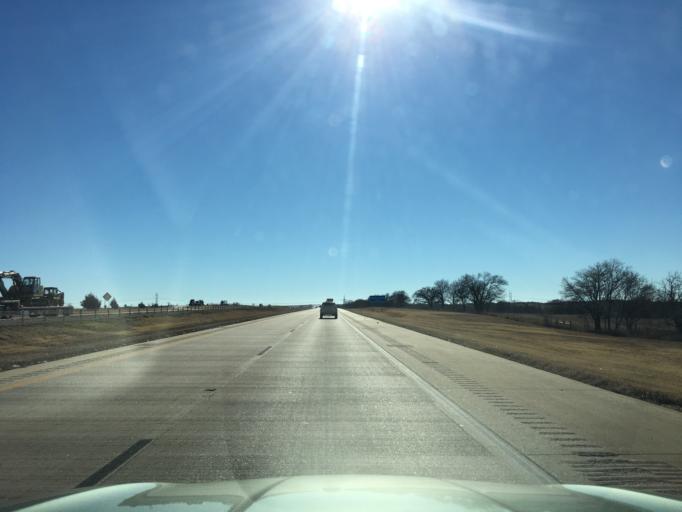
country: US
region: Oklahoma
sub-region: Noble County
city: Perry
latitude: 36.4317
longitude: -97.3271
